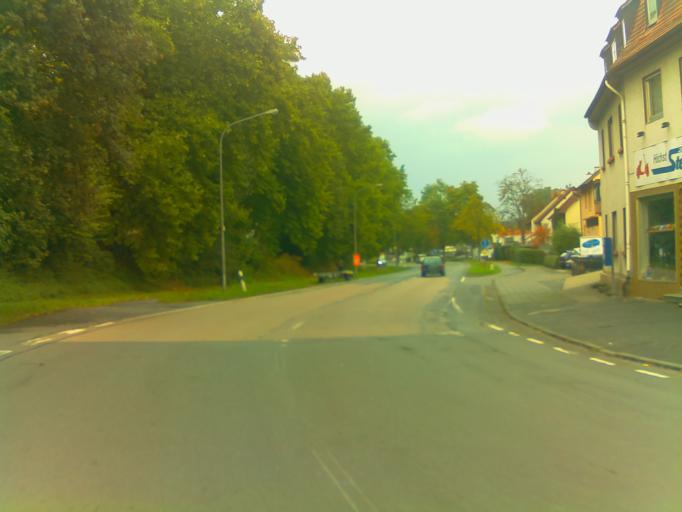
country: DE
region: Hesse
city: Hochst im Odenwald
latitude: 49.8032
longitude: 8.9978
